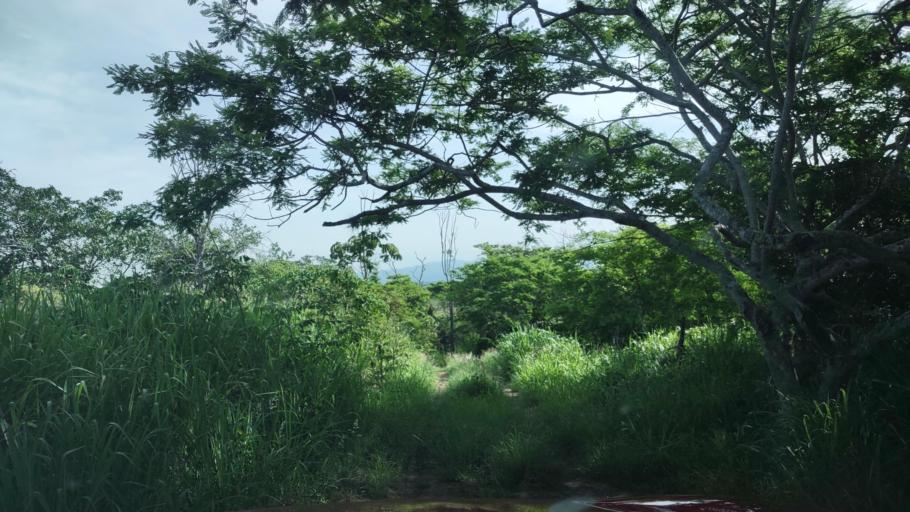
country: MX
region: Veracruz
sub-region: Emiliano Zapata
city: Dos Rios
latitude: 19.4764
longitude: -96.8278
